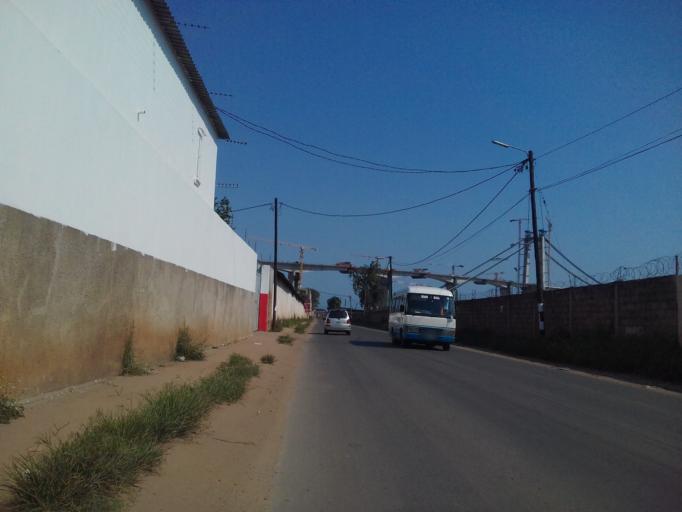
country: MZ
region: Maputo City
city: Maputo
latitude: -25.9613
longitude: 32.5562
